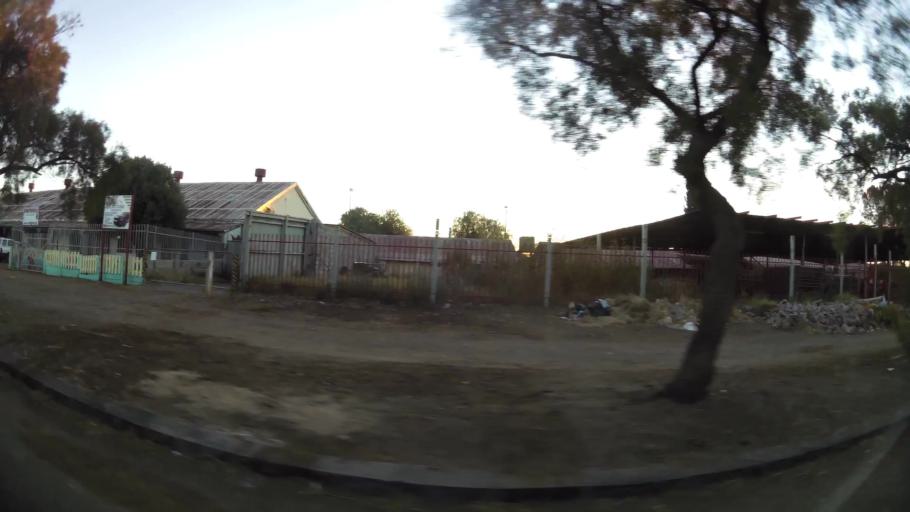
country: ZA
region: Northern Cape
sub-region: Frances Baard District Municipality
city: Kimberley
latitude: -28.7335
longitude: 24.7717
